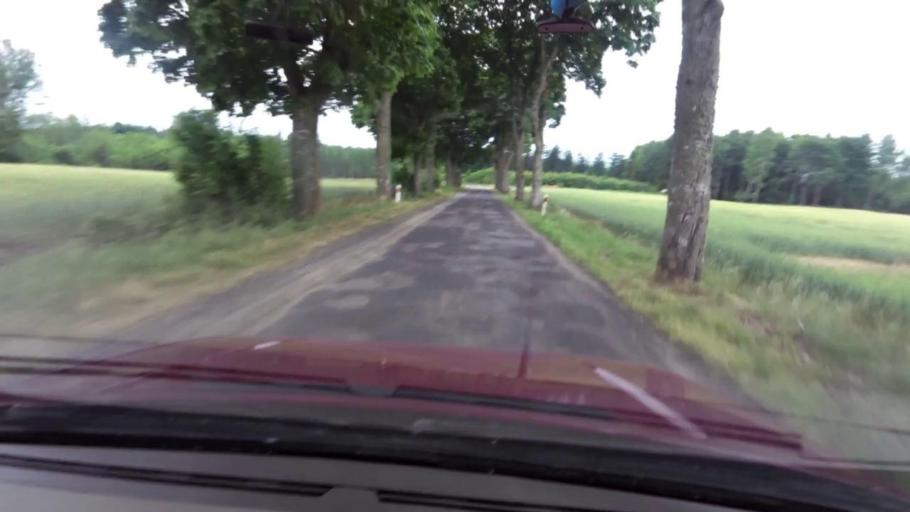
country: PL
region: Pomeranian Voivodeship
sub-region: Powiat slupski
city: Kepice
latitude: 54.1810
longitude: 16.7894
